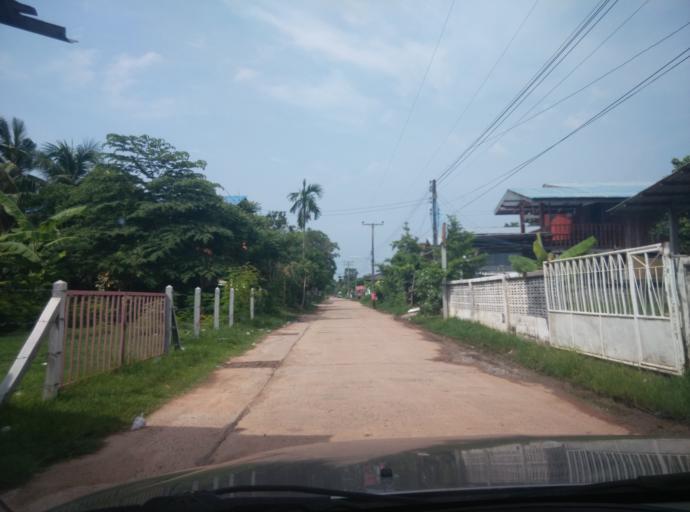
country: TH
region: Sisaket
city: Huai Thap Than
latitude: 15.0513
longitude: 104.0830
